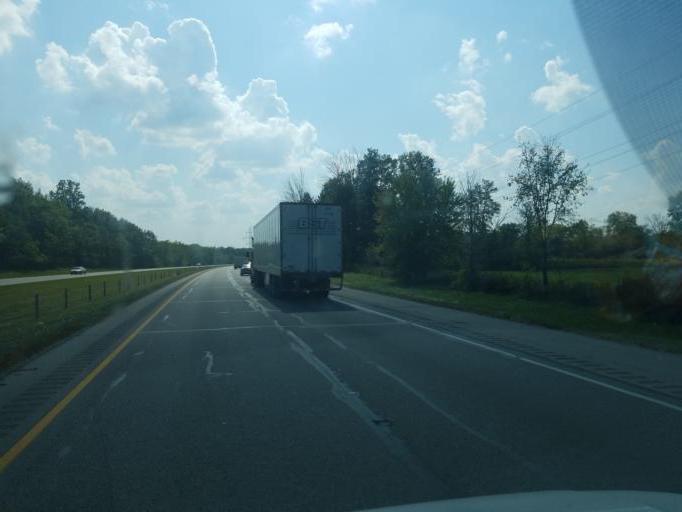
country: US
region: Indiana
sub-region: Allen County
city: Leo-Cedarville
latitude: 41.2419
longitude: -85.0923
